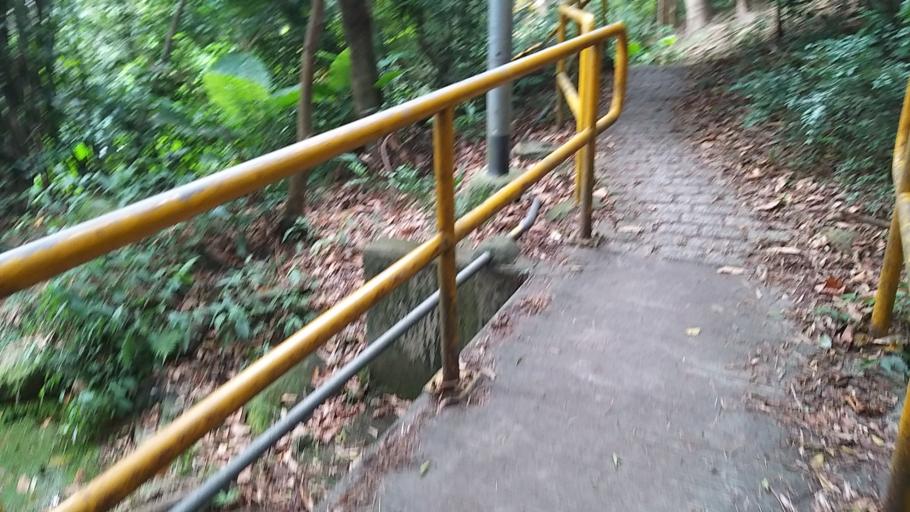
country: HK
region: Tuen Mun
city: Tuen Mun
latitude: 22.3833
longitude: 113.9830
